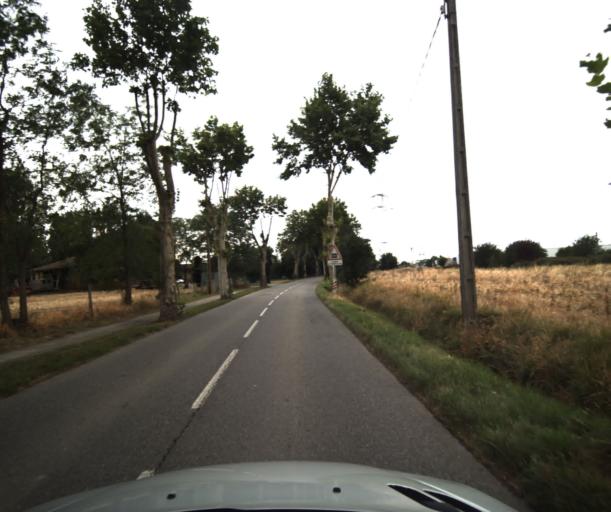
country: FR
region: Midi-Pyrenees
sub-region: Departement de la Haute-Garonne
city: Portet-sur-Garonne
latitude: 43.5305
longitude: 1.3937
